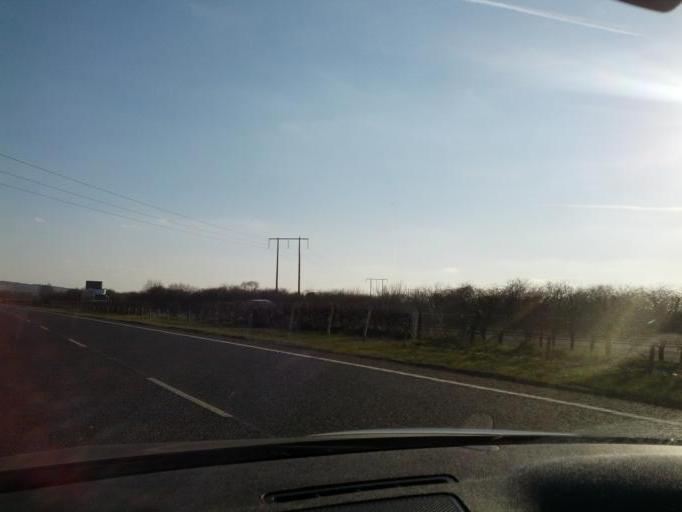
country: IE
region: Leinster
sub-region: Laois
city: Portlaoise
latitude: 53.0431
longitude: -7.2433
